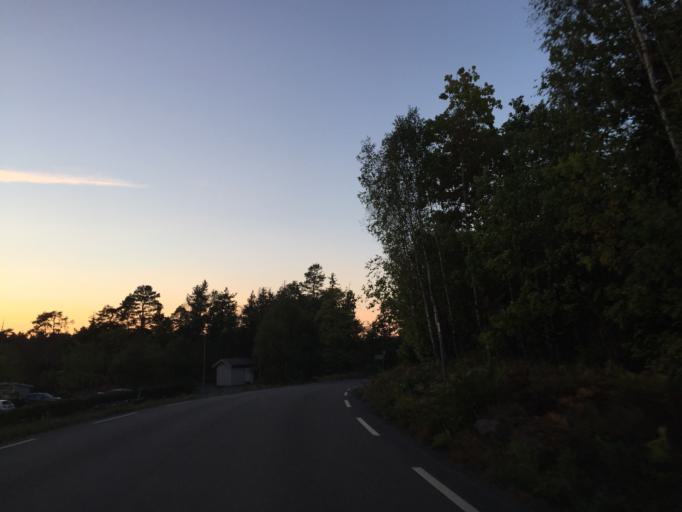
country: NO
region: Ostfold
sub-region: Moss
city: Moss
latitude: 59.4891
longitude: 10.6913
